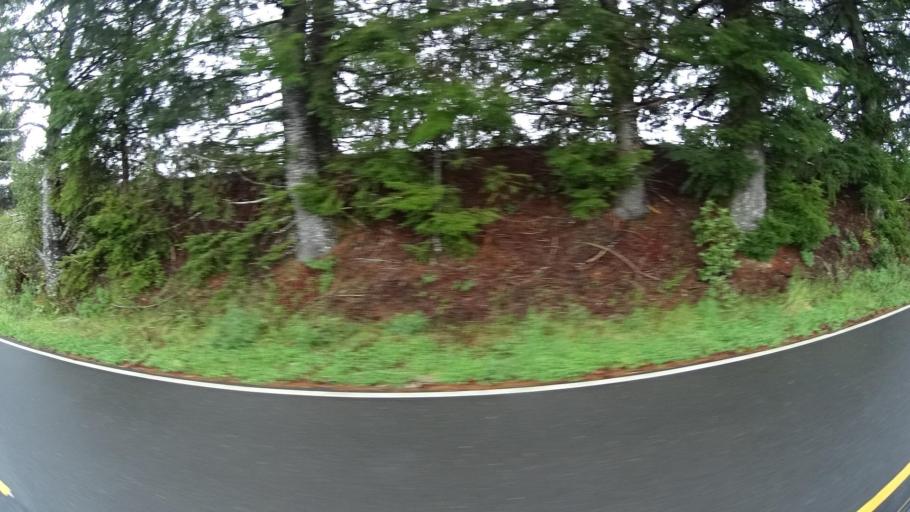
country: US
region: California
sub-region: Humboldt County
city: Westhaven-Moonstone
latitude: 41.1737
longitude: -123.9202
